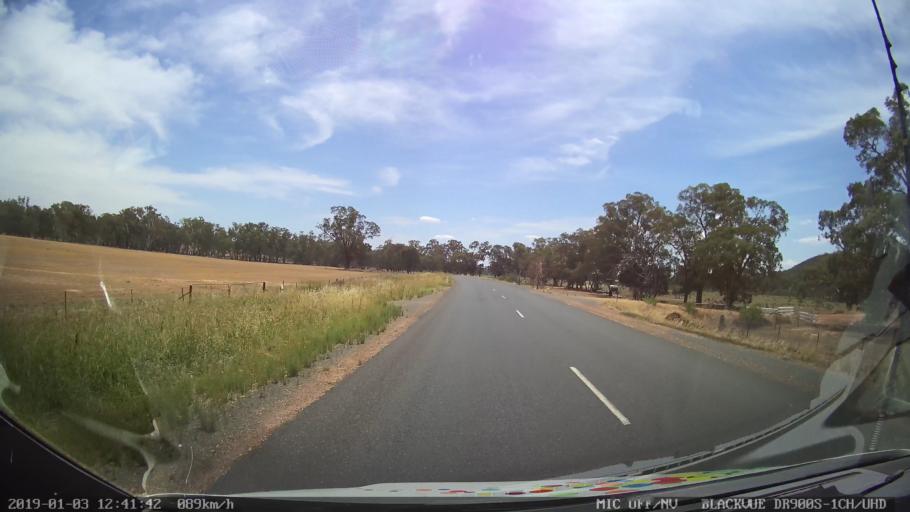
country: AU
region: New South Wales
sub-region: Weddin
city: Grenfell
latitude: -33.7962
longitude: 148.2153
